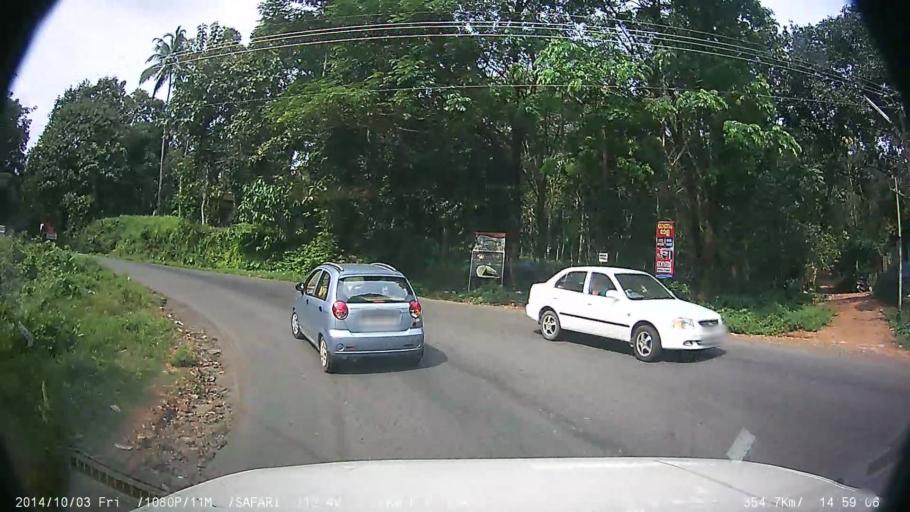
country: IN
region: Kerala
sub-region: Kottayam
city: Palackattumala
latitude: 9.8109
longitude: 76.5773
